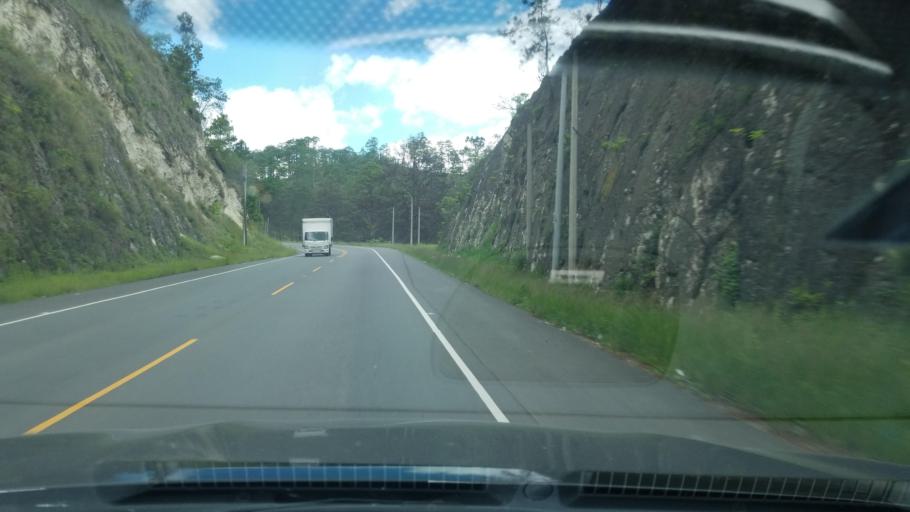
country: HN
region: Francisco Morazan
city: Talanga
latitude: 14.3598
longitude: -87.1469
